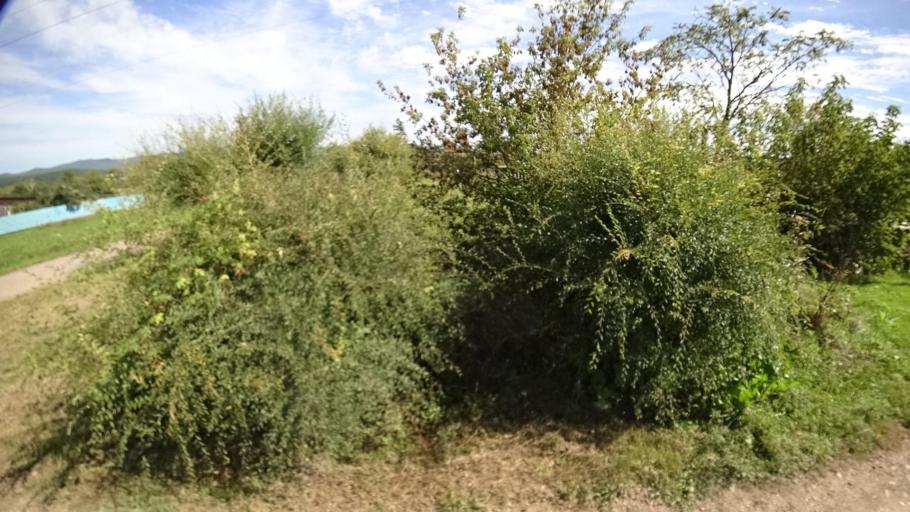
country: RU
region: Primorskiy
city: Yakovlevka
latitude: 44.4304
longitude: 133.5614
